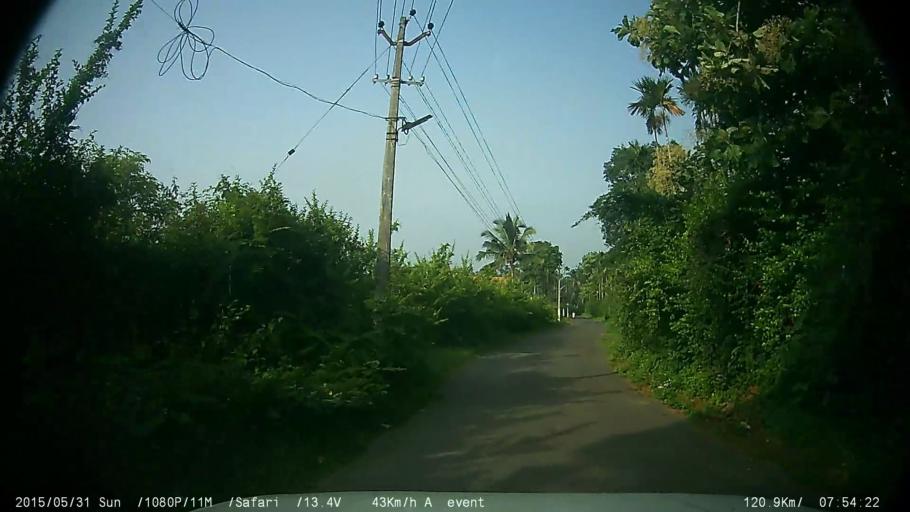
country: IN
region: Kerala
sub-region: Wayanad
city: Kalpetta
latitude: 11.6385
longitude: 76.0812
